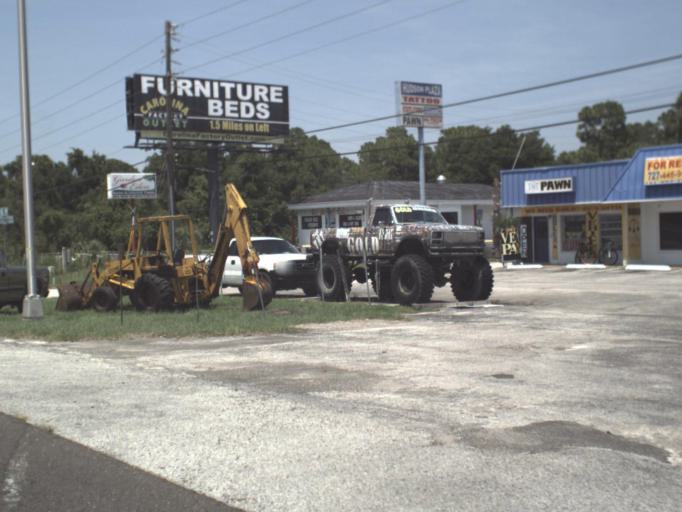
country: US
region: Florida
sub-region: Pasco County
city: Hudson
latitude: 28.3529
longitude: -82.6990
